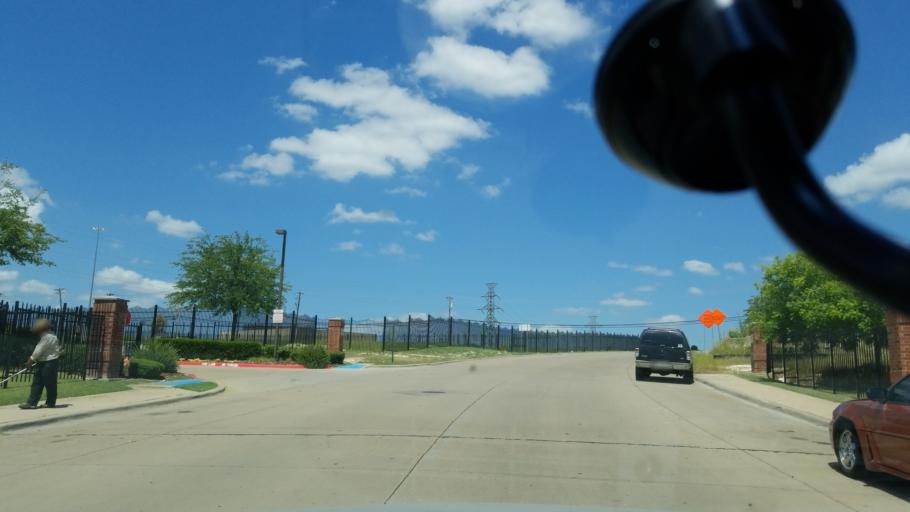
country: US
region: Texas
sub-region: Dallas County
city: Cockrell Hill
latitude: 32.7006
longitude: -96.8263
